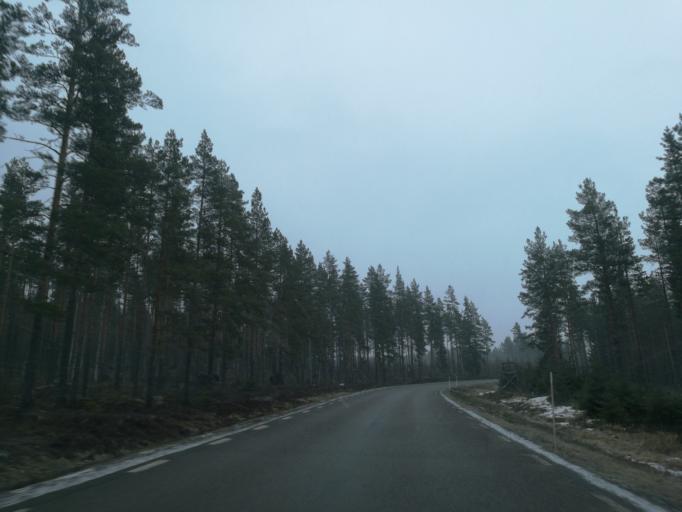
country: NO
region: Hedmark
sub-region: Asnes
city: Flisa
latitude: 60.6994
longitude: 12.5211
